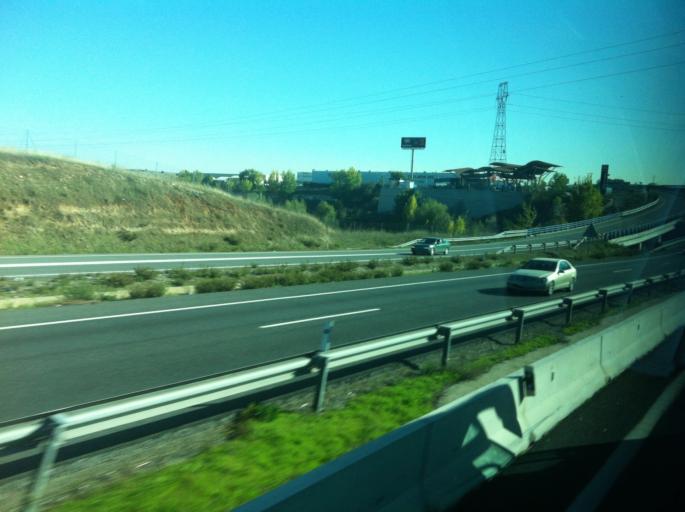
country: ES
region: Madrid
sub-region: Provincia de Madrid
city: San Agustin de Guadalix
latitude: 40.6756
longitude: -3.6113
